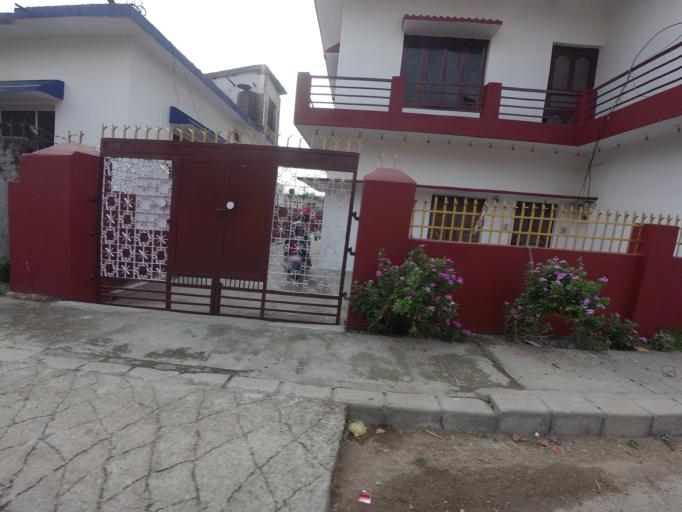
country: NP
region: Western Region
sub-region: Lumbini Zone
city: Bhairahawa
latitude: 27.4967
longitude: 83.4496
